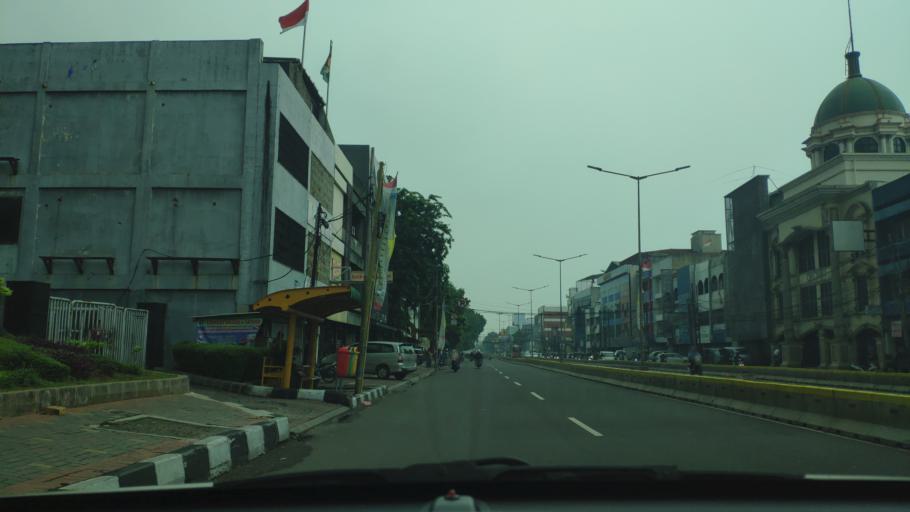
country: ID
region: Jakarta Raya
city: Jakarta
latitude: -6.1654
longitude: 106.8154
